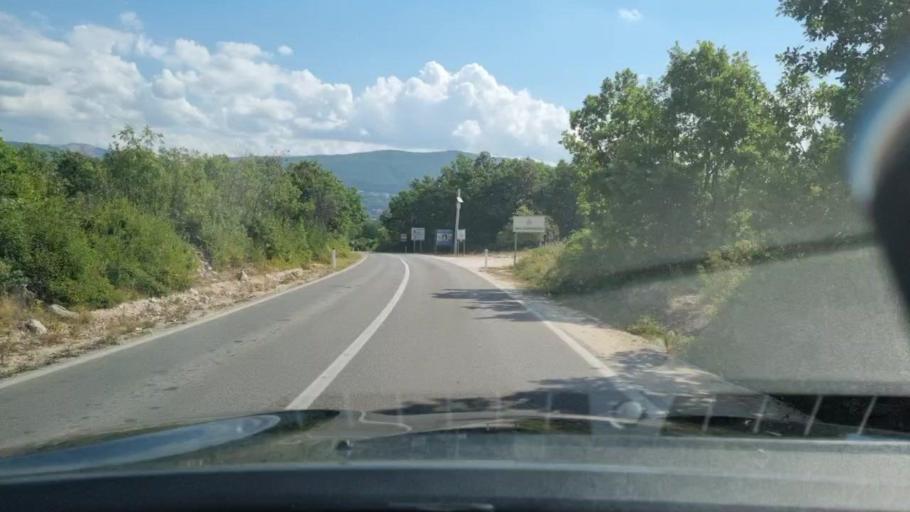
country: BA
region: Federation of Bosnia and Herzegovina
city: Dreznica
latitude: 43.4606
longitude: 17.2868
